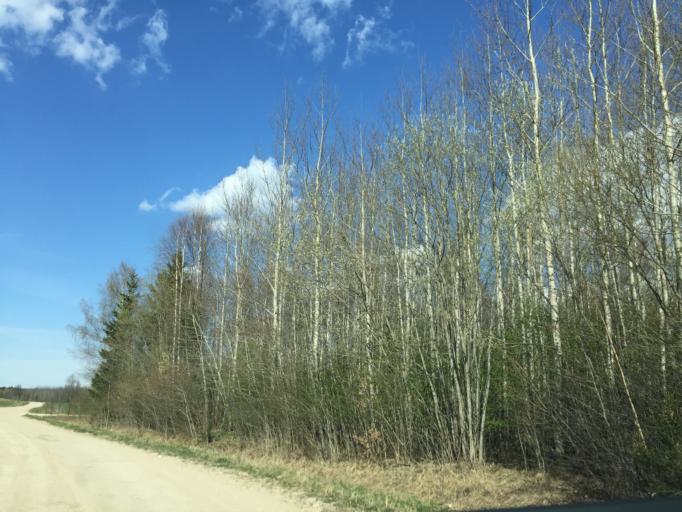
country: LV
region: Lielvarde
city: Lielvarde
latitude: 56.8284
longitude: 24.7957
